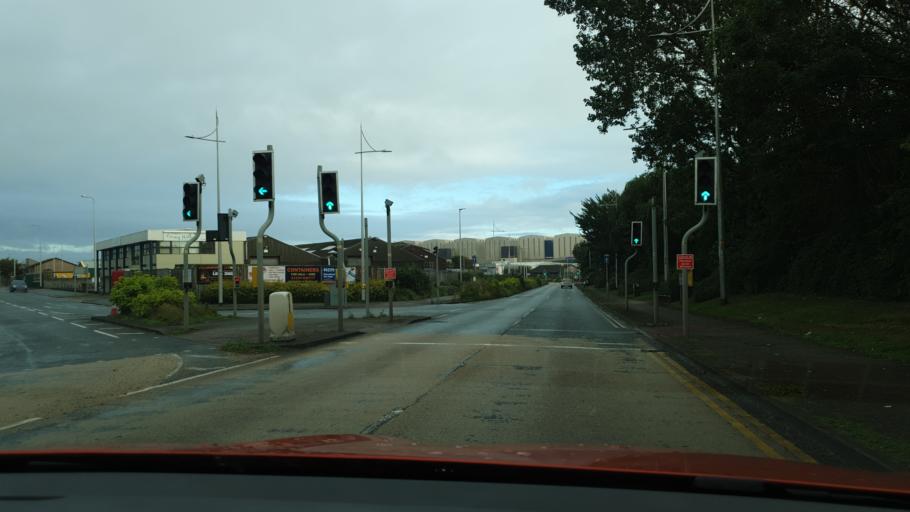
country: GB
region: England
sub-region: Cumbria
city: Barrow in Furness
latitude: 54.1185
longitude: -3.2383
